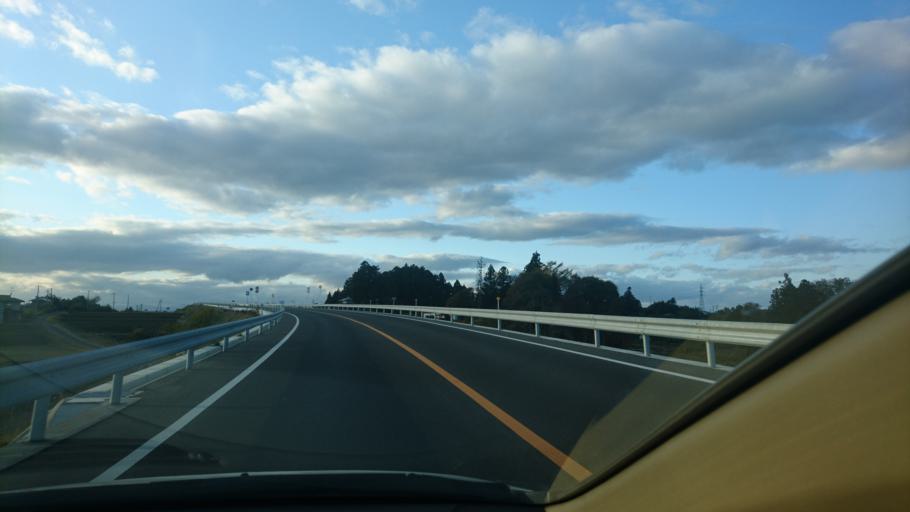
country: JP
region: Miyagi
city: Kogota
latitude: 38.7361
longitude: 141.0513
